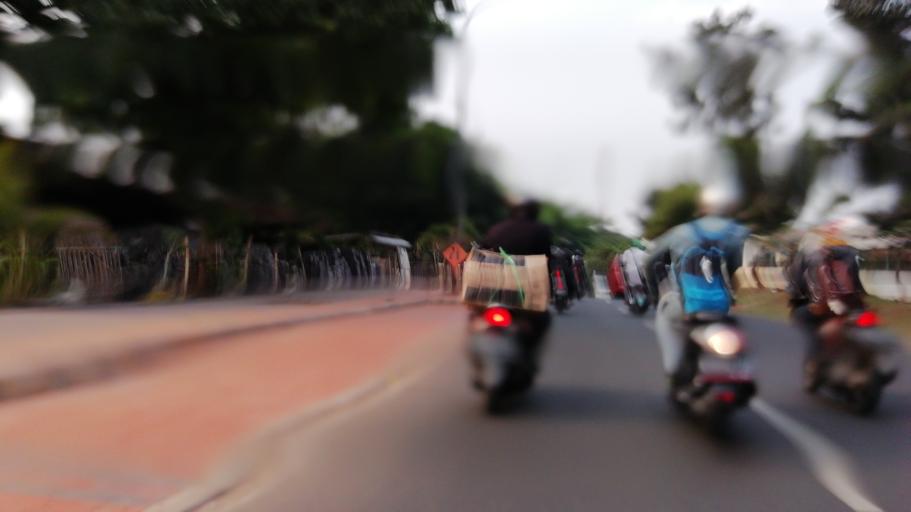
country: ID
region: West Java
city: Depok
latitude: -6.3491
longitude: 106.8326
